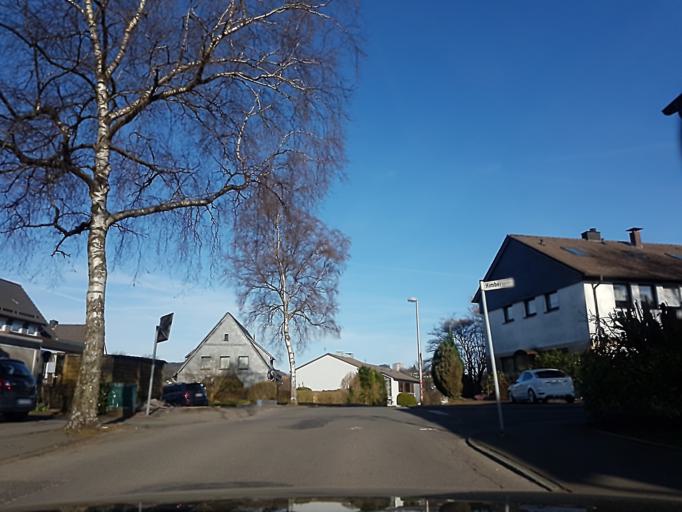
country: DE
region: North Rhine-Westphalia
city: Meinerzhagen
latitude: 51.1054
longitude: 7.6468
